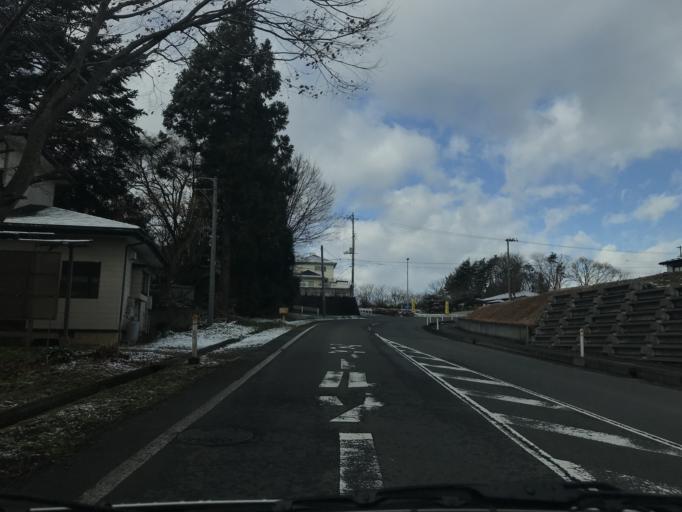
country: JP
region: Iwate
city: Mizusawa
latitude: 39.1090
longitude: 141.1370
